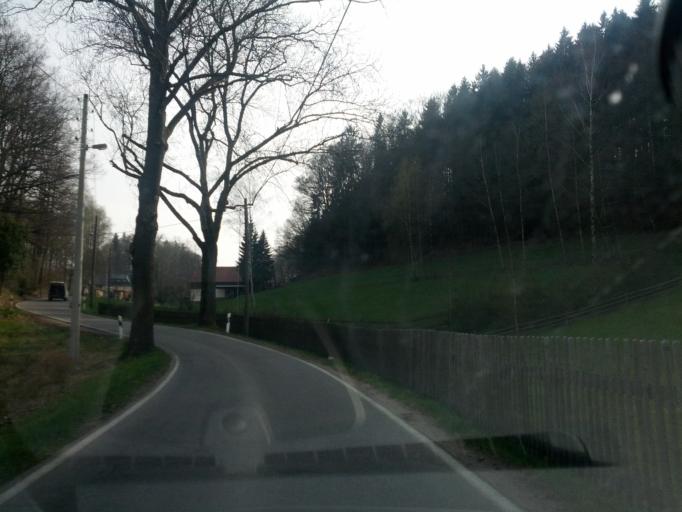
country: DE
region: Saxony
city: Kirchberg
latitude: 50.5891
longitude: 12.5153
